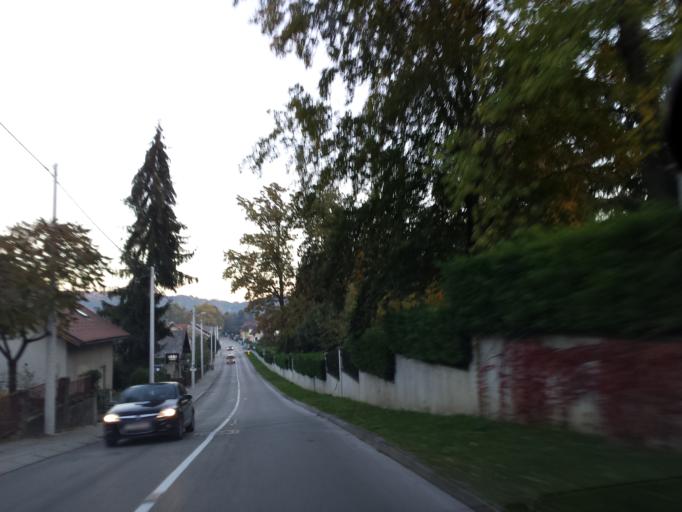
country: HR
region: Zagrebacka
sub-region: Grad Samobor
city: Samobor
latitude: 45.7987
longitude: 15.7162
